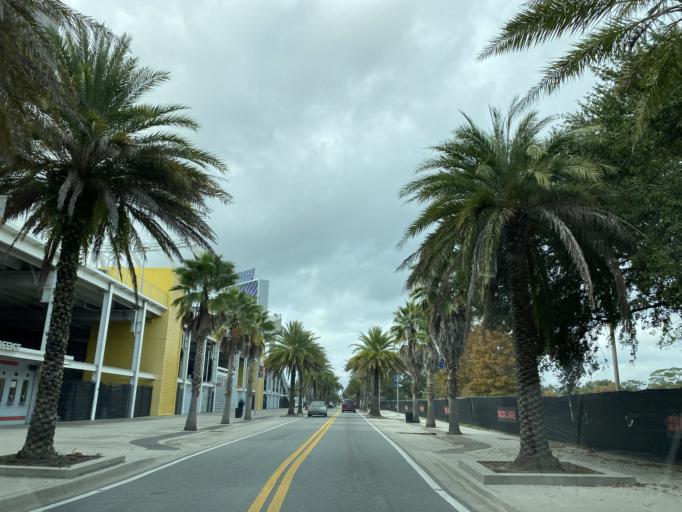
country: US
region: Florida
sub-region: Orange County
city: Orlando
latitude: 28.5402
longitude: -81.4020
